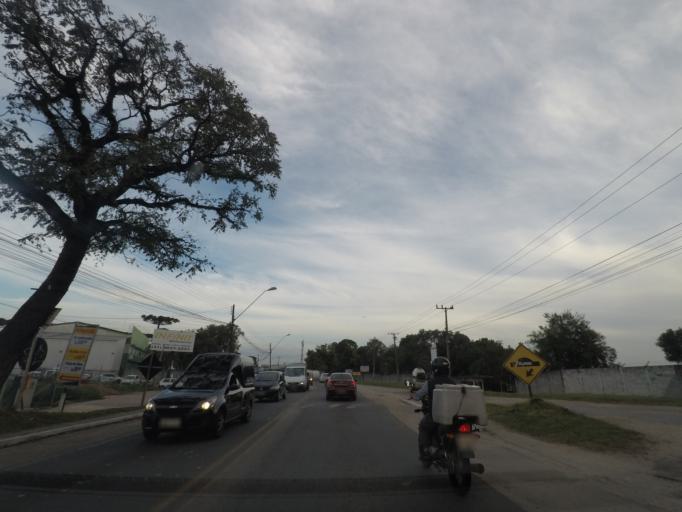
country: BR
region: Parana
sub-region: Colombo
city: Colombo
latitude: -25.3495
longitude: -49.2214
